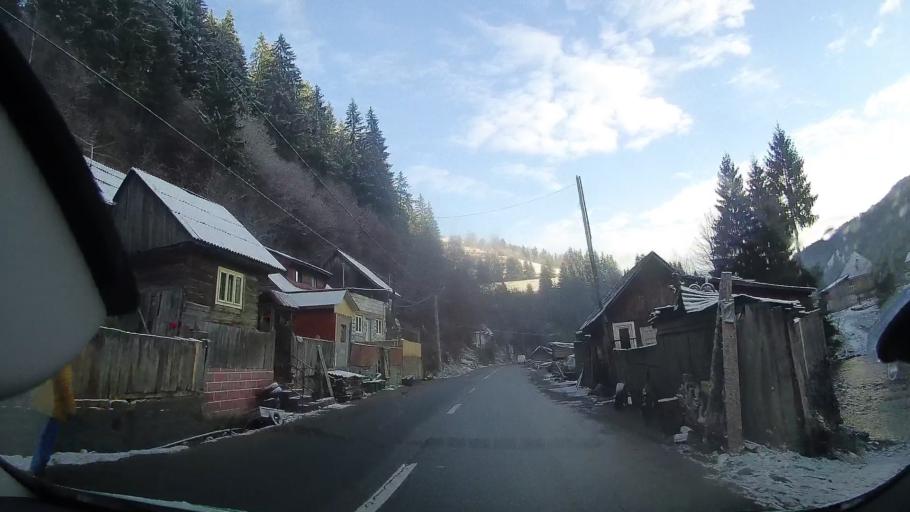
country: RO
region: Alba
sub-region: Comuna Scarisoara
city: Scarisoara
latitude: 46.4570
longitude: 22.8679
